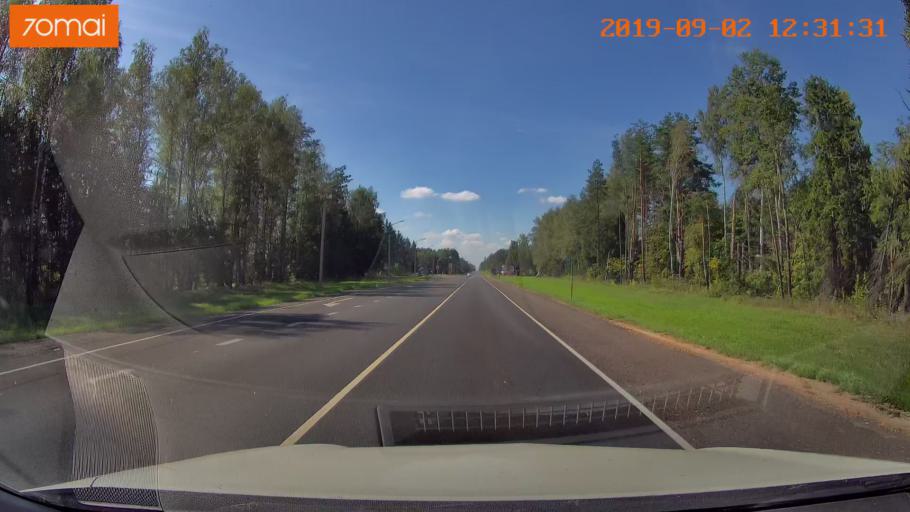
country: RU
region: Smolensk
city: Shumyachi
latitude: 53.8238
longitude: 32.4479
